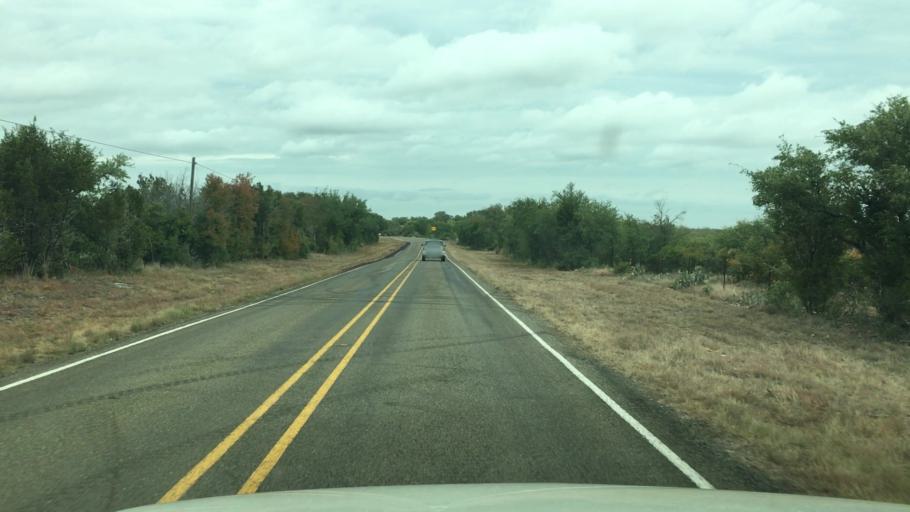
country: US
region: Texas
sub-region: Llano County
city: Horseshoe Bay
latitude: 30.4753
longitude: -98.4165
